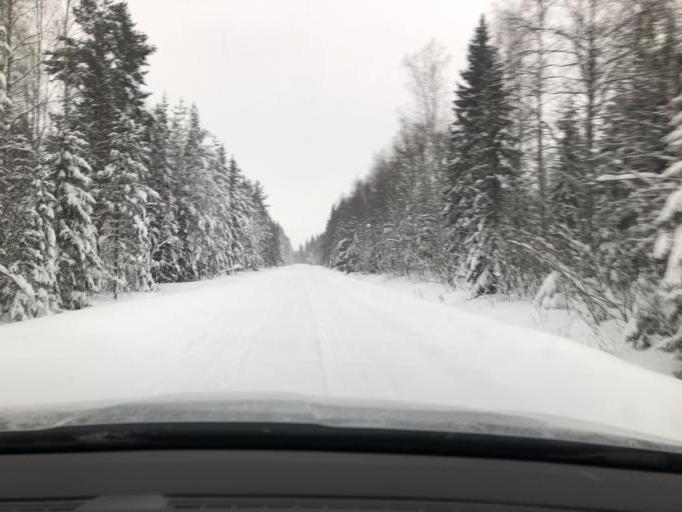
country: SE
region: Vaesterbotten
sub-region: Umea Kommun
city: Saevar
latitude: 63.9400
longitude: 20.7121
